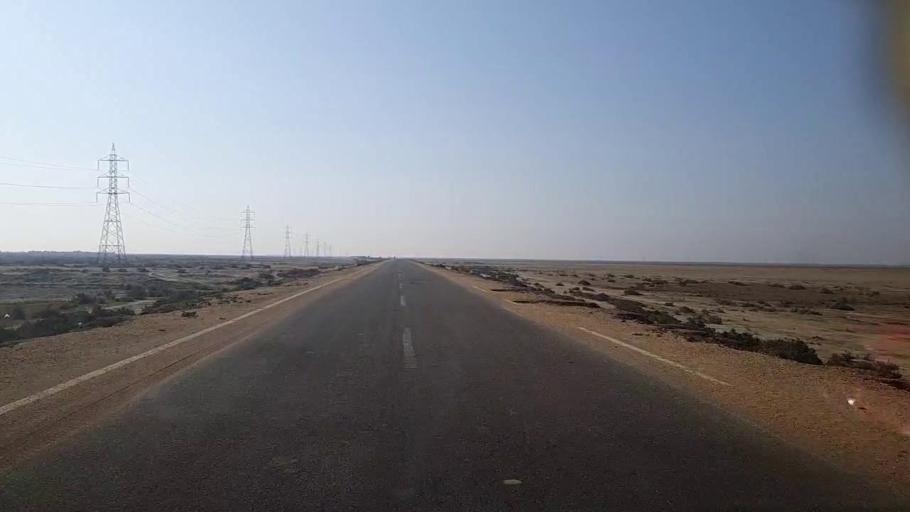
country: PK
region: Sindh
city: Mirpur Sakro
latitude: 24.6140
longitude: 67.4970
